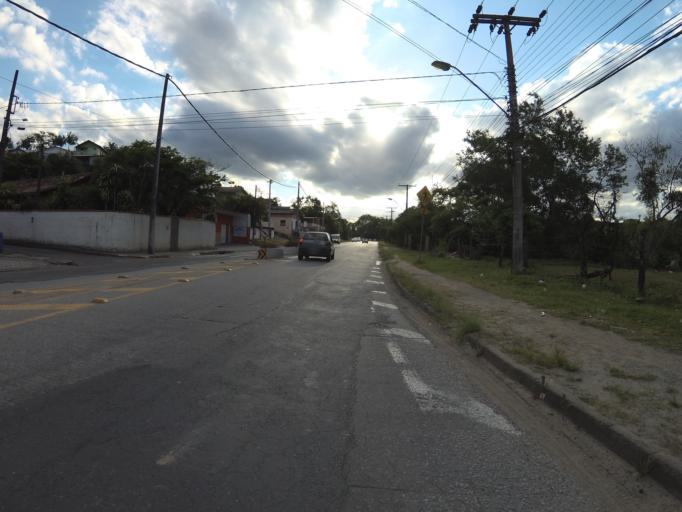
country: BR
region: Santa Catarina
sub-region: Blumenau
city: Blumenau
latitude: -26.8843
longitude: -49.1098
